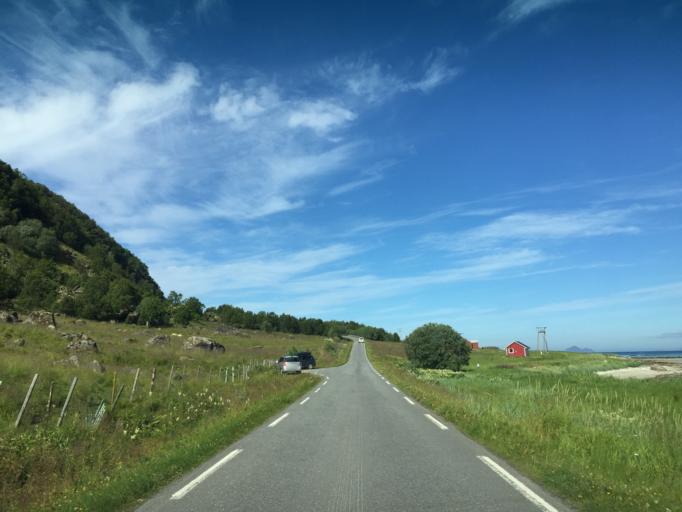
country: NO
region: Nordland
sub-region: Vagan
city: Svolvaer
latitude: 68.3984
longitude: 14.5311
